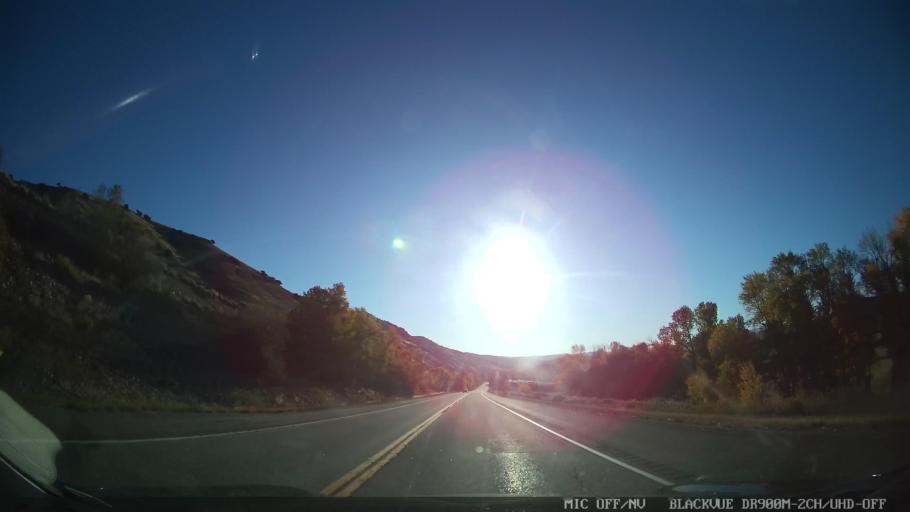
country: US
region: Colorado
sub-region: Grand County
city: Hot Sulphur Springs
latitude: 40.0662
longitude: -106.2000
